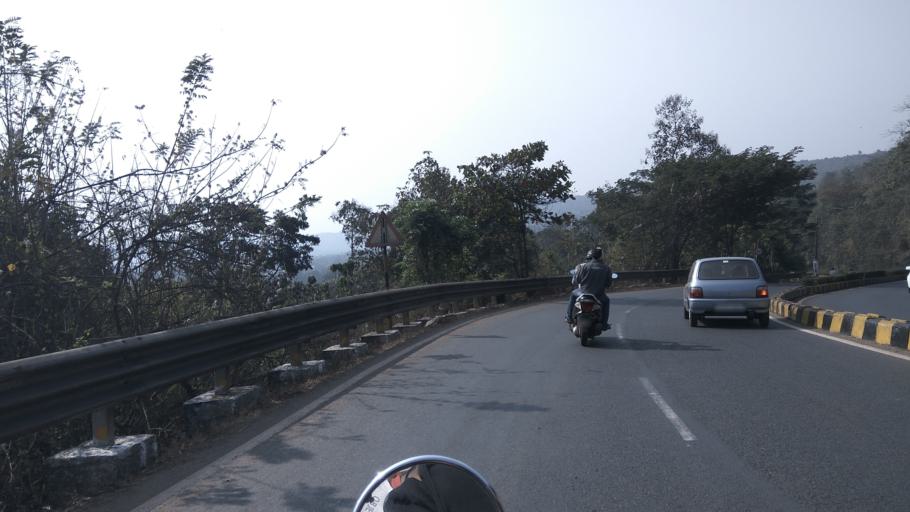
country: IN
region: Goa
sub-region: North Goa
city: Bandora
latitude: 15.4548
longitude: 73.9664
